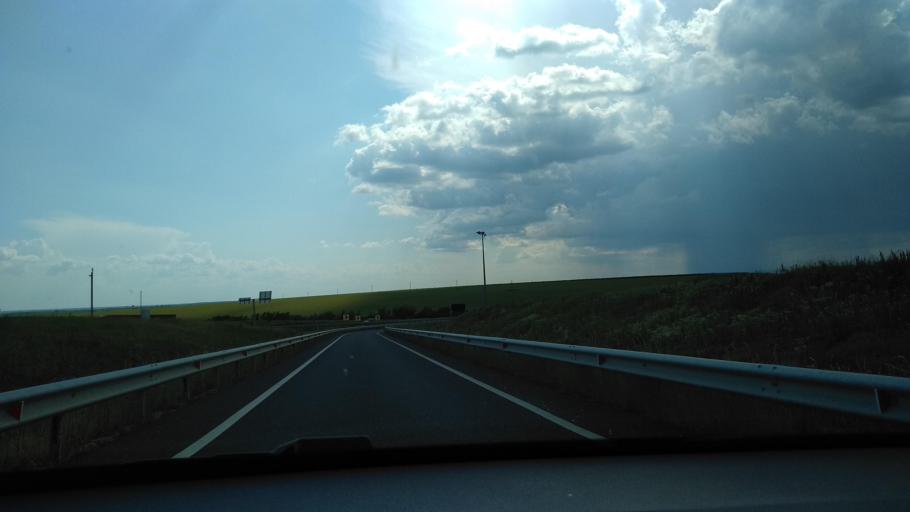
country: RO
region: Timis
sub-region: Comuna Topolovatu Mare
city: Topolovatu Mare
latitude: 45.8020
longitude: 21.6578
